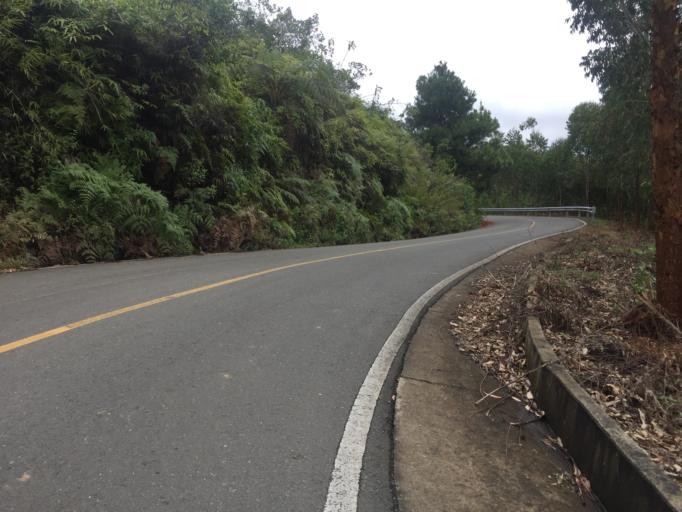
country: CO
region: Valle del Cauca
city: Dagua
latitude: 3.7042
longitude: -76.5873
